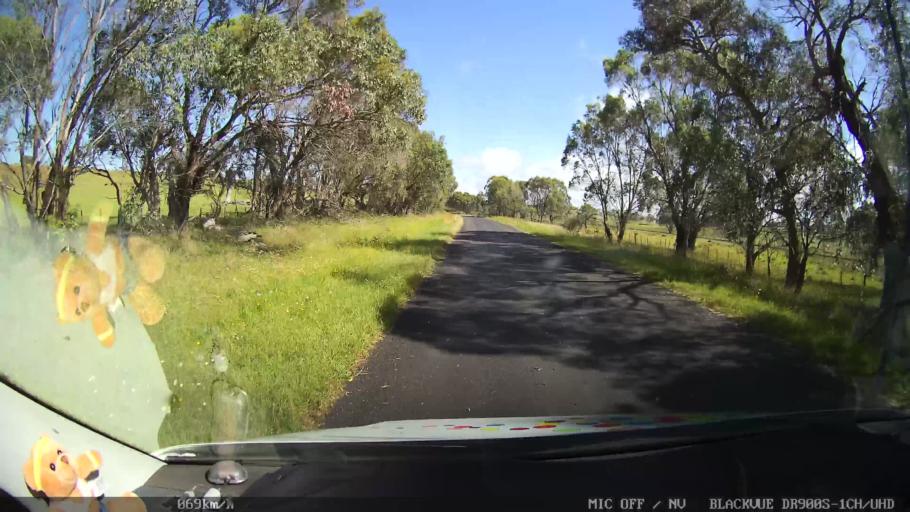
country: AU
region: New South Wales
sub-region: Guyra
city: Guyra
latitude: -30.0817
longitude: 151.6773
